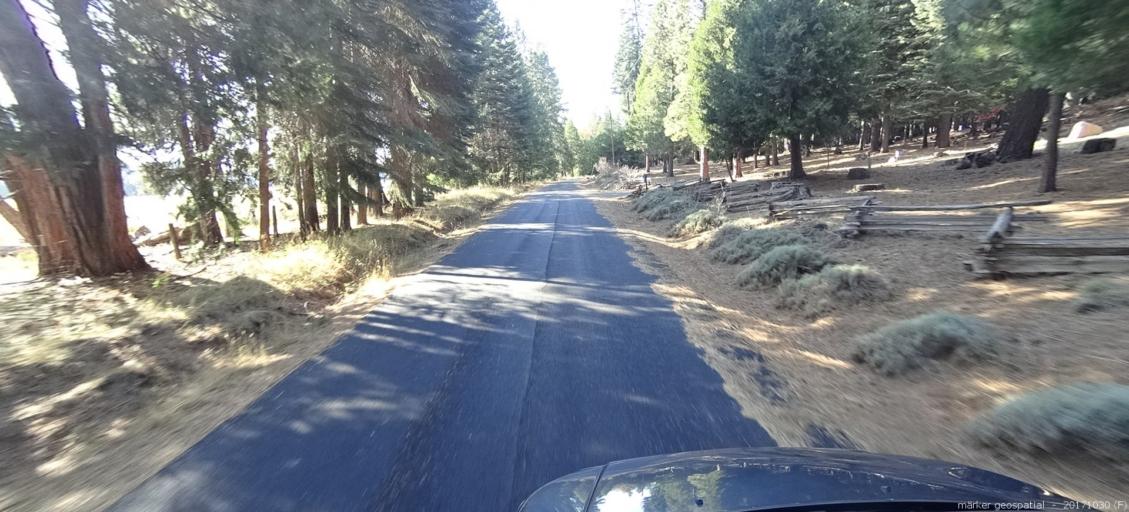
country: US
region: California
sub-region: Shasta County
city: Shingletown
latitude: 40.5310
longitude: -121.6994
